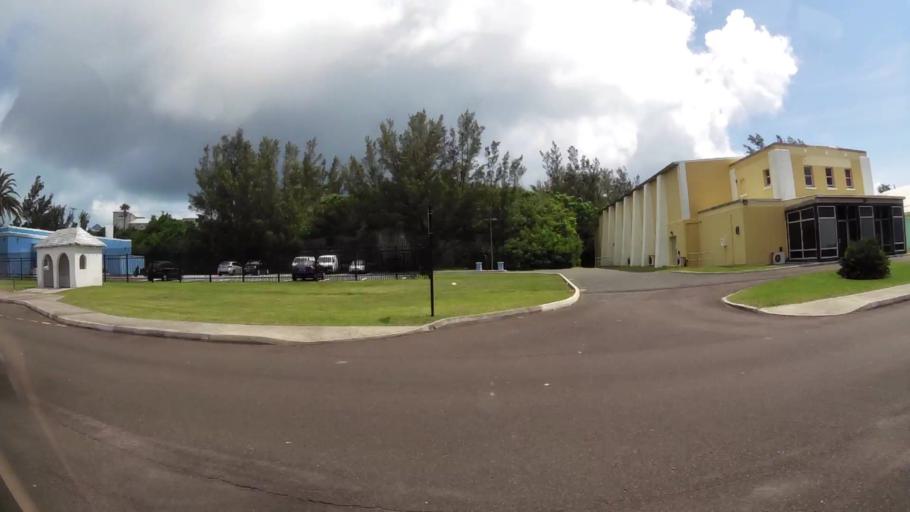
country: BM
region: Saint George
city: Saint George
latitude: 32.3657
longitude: -64.6682
